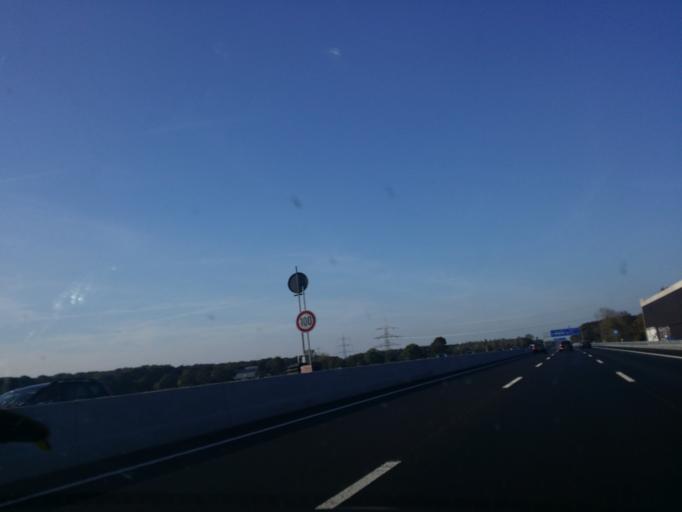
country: DE
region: North Rhine-Westphalia
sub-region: Regierungsbezirk Munster
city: Senden
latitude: 51.8972
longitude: 7.5707
